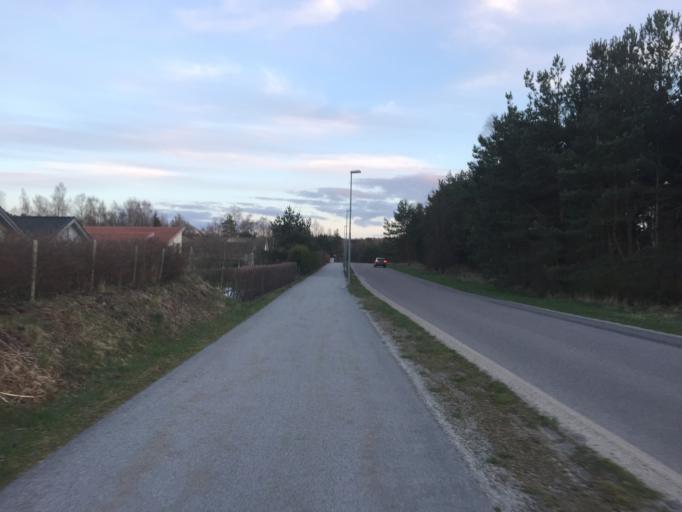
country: SE
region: Skane
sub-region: Lunds Kommun
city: Veberod
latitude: 55.6267
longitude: 13.4989
